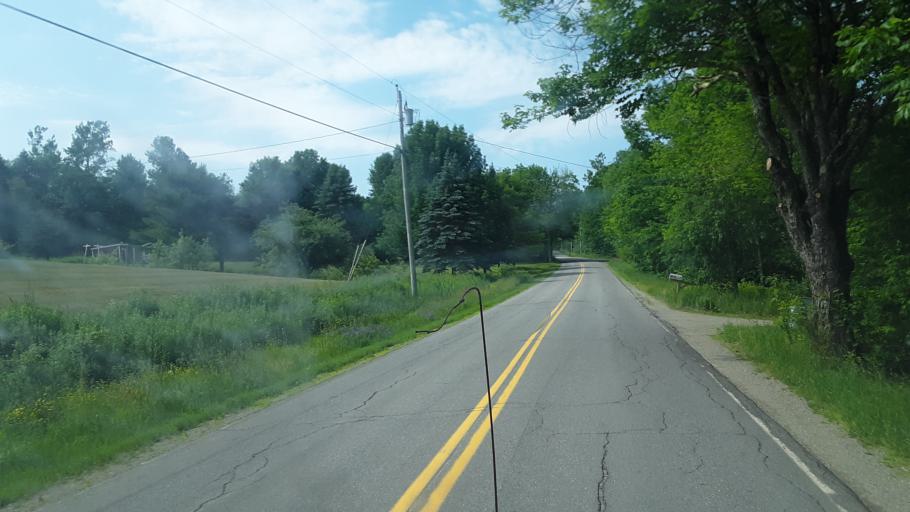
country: US
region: Maine
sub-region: Waldo County
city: Frankfort
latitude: 44.5872
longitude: -68.9447
